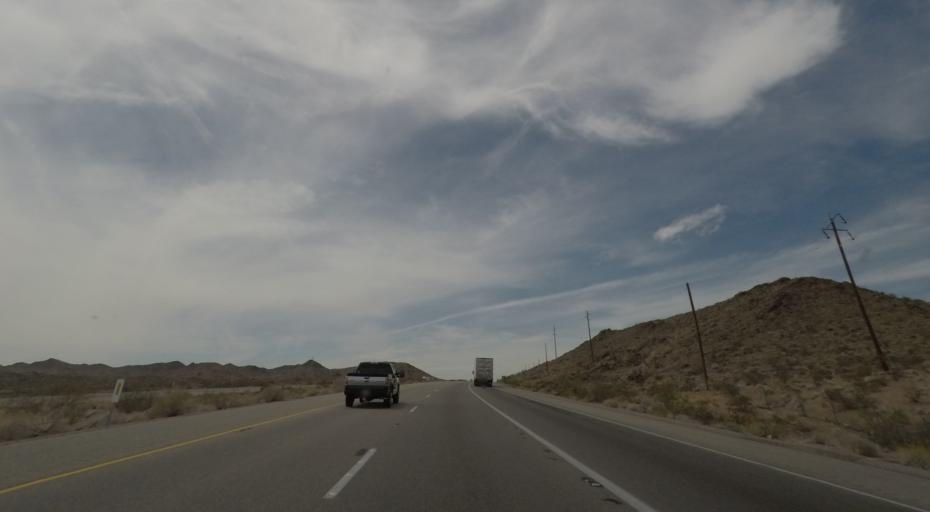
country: US
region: California
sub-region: San Bernardino County
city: Needles
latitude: 34.8295
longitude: -115.0297
